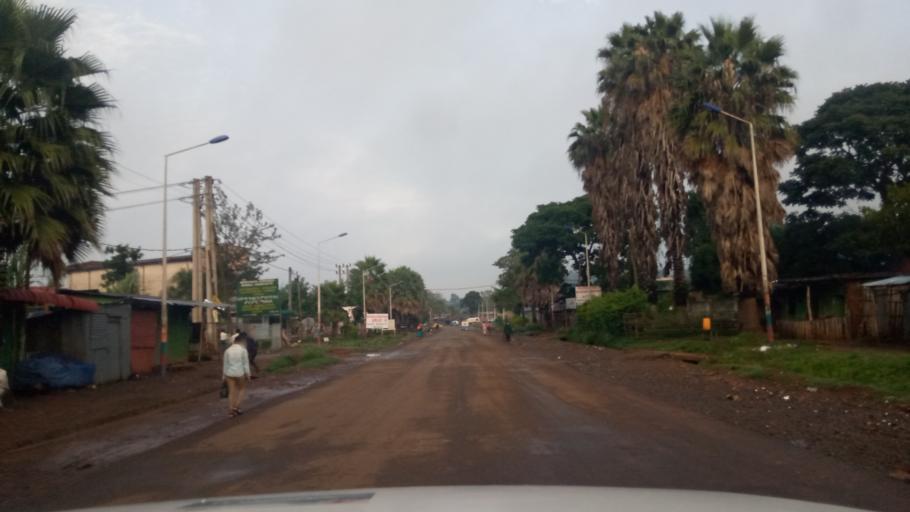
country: ET
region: Oromiya
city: Jima
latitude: 7.6832
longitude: 36.8443
